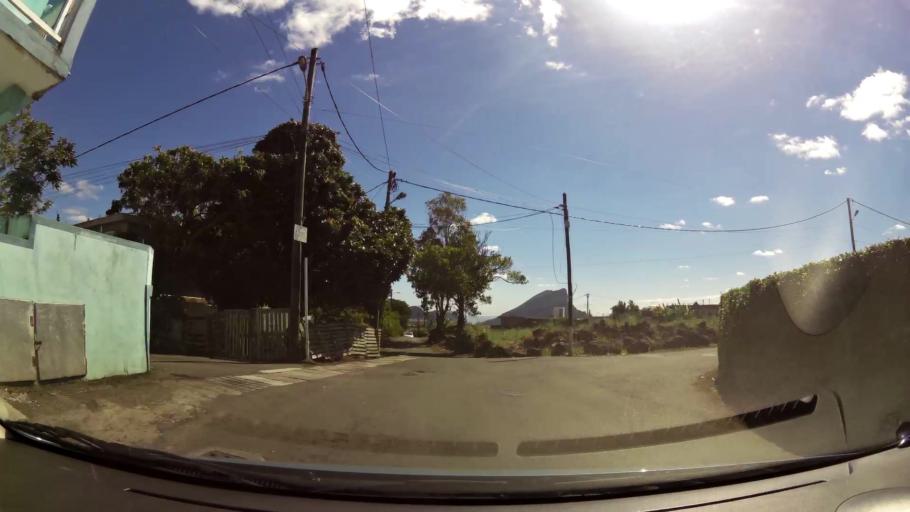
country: MU
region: Plaines Wilhems
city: Vacoas
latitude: -20.3102
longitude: 57.4723
